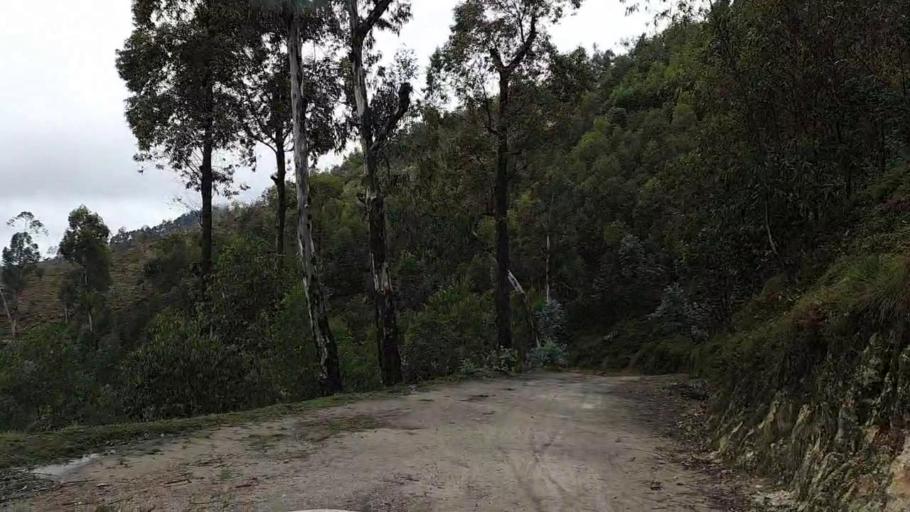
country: RW
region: Southern Province
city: Gikongoro
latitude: -2.3665
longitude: 29.4956
